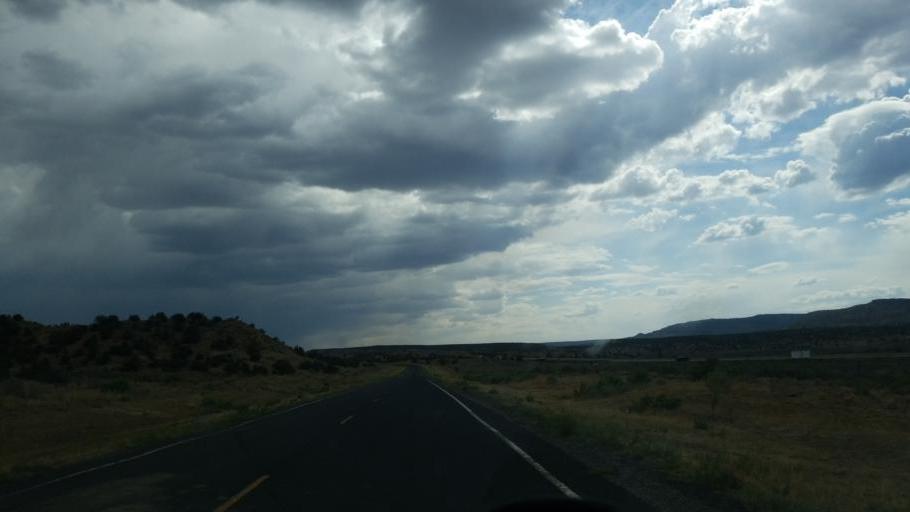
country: US
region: Arizona
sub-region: Apache County
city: Saint Michaels
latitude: 35.4294
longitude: -108.9713
